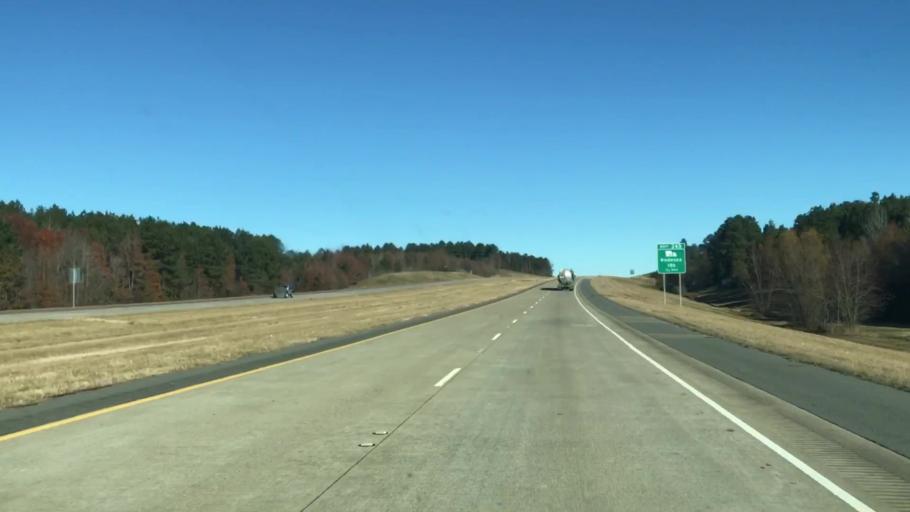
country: US
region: Louisiana
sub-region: Caddo Parish
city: Vivian
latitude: 32.9844
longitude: -93.9105
